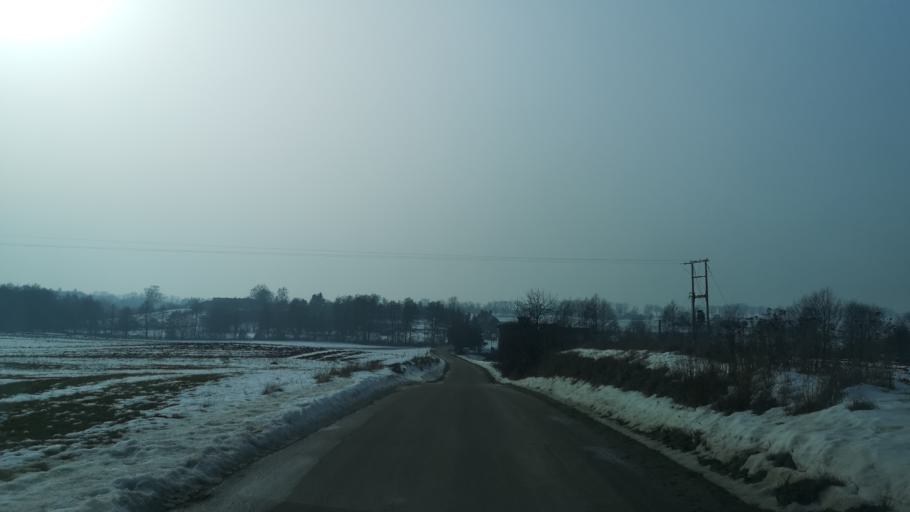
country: PL
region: Warmian-Masurian Voivodeship
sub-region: Powiat nowomiejski
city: Biskupiec
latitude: 53.5311
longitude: 19.3586
